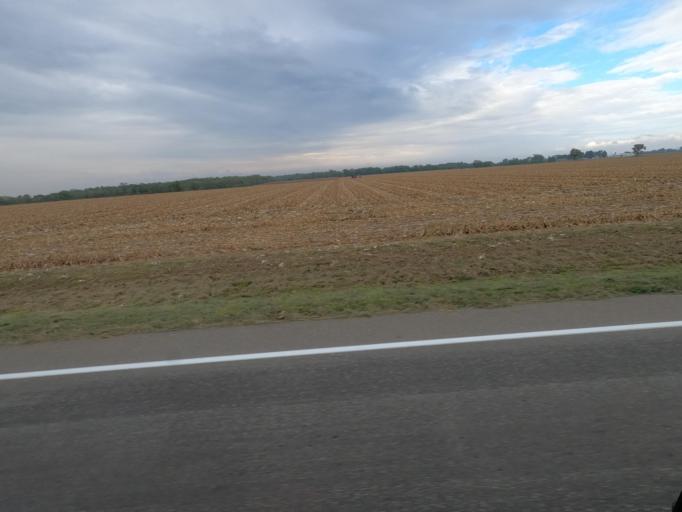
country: US
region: Iowa
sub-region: Henry County
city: Mount Pleasant
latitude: 40.7846
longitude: -91.6682
